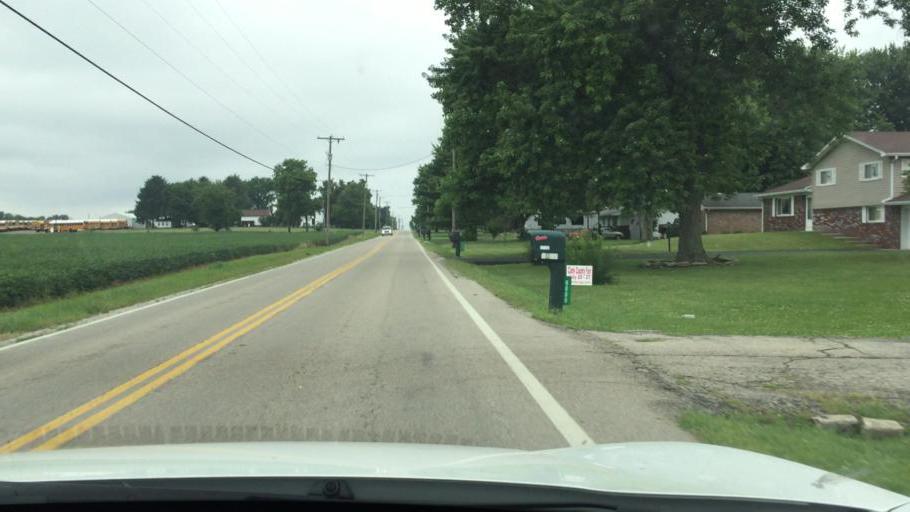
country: US
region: Ohio
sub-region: Clark County
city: Lisbon
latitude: 39.9419
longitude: -83.6747
